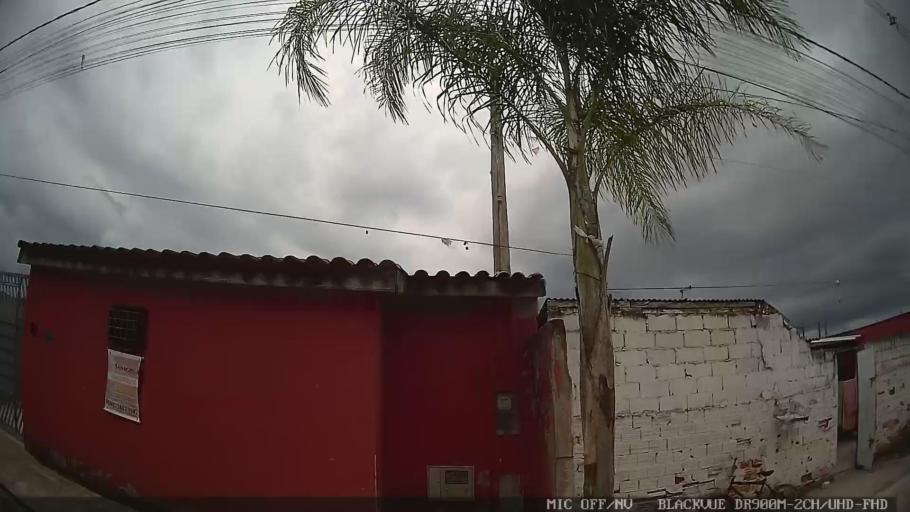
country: BR
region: Sao Paulo
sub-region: Caraguatatuba
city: Caraguatatuba
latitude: -23.6732
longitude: -45.4543
